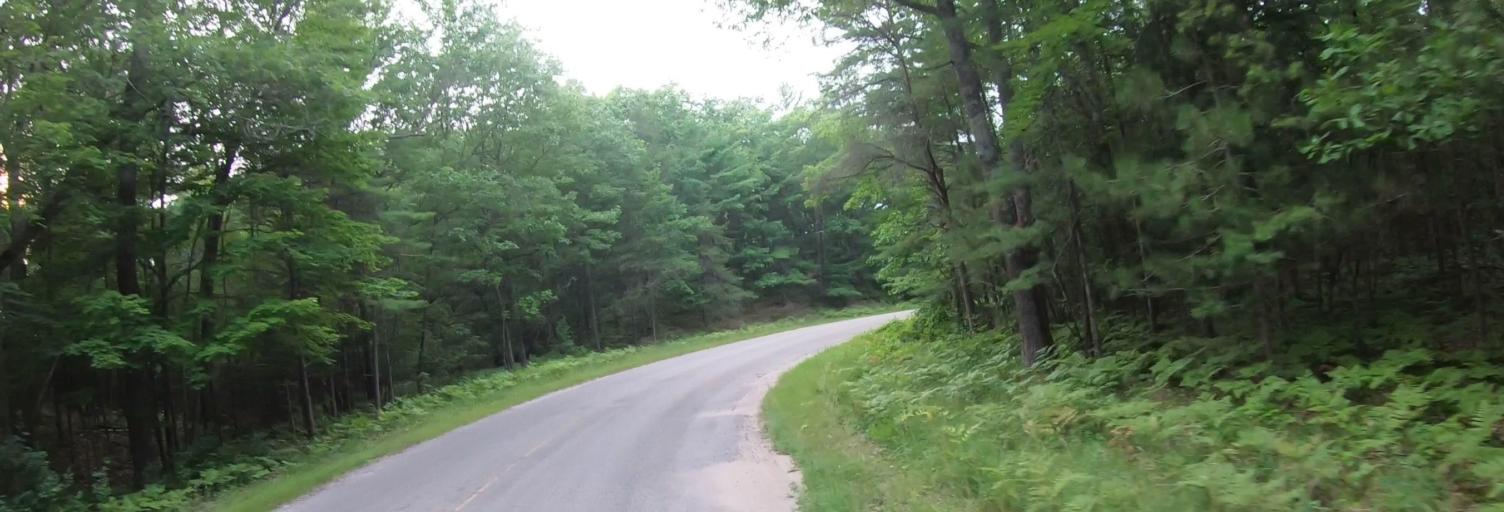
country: US
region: Michigan
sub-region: Emmet County
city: Harbor Springs
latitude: 45.6804
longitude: -84.9724
